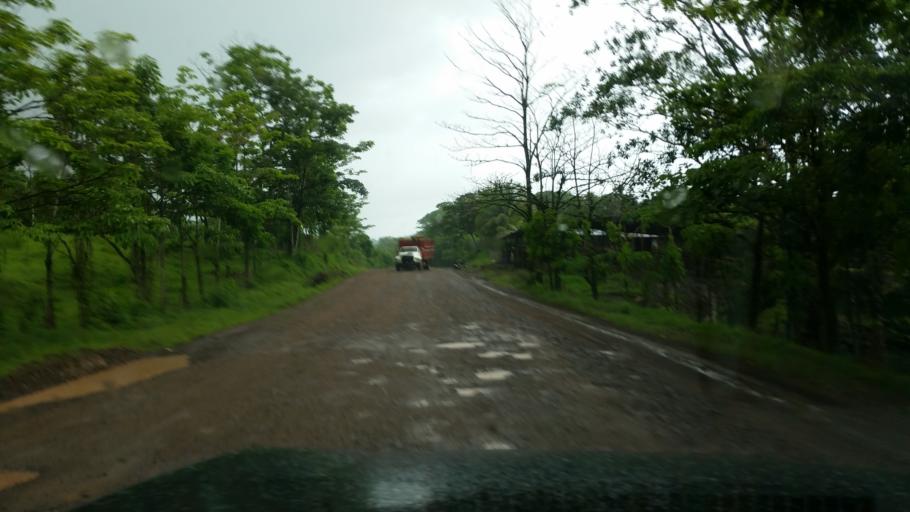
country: NI
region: Atlantico Norte (RAAN)
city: Siuna
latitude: 13.4057
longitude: -84.8539
